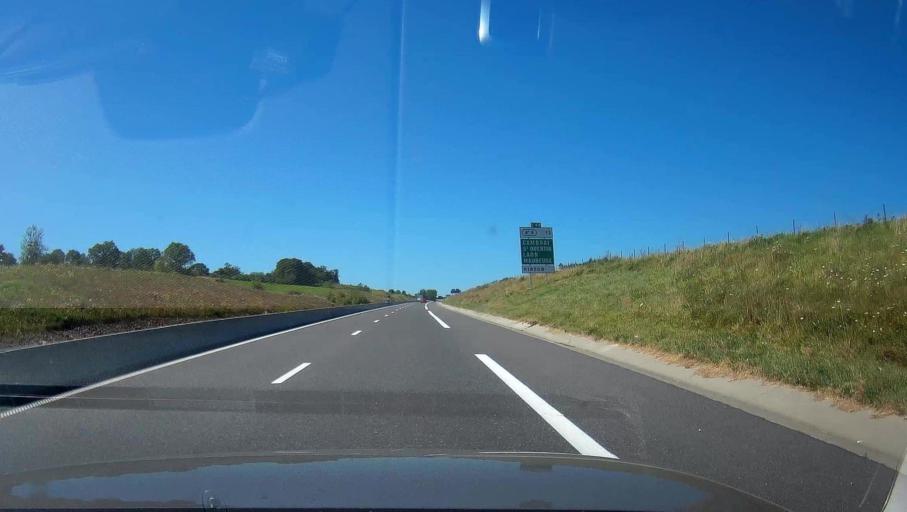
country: FR
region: Champagne-Ardenne
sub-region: Departement des Ardennes
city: Tournes
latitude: 49.7701
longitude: 4.6307
